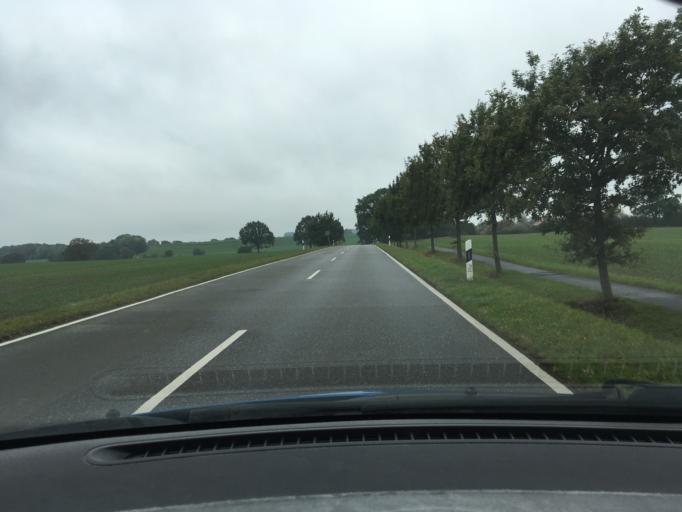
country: DE
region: Schleswig-Holstein
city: Bosdorf
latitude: 54.1311
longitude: 10.4784
